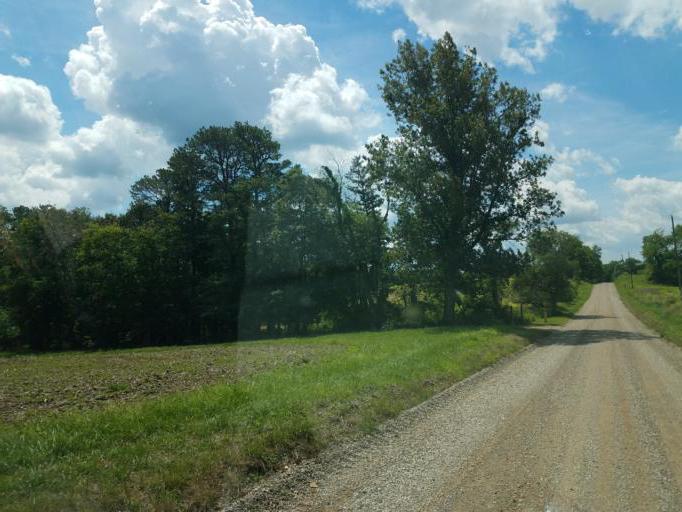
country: US
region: Ohio
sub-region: Knox County
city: Danville
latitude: 40.4125
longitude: -82.2919
